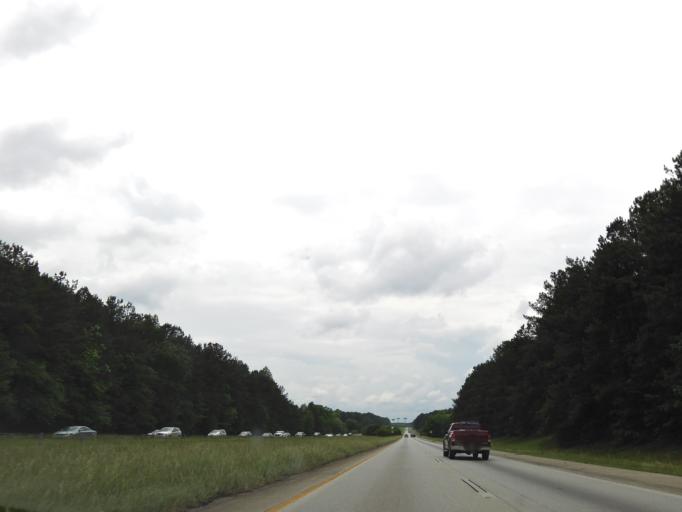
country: US
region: Georgia
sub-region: Carroll County
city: Temple
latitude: 33.7168
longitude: -84.9919
